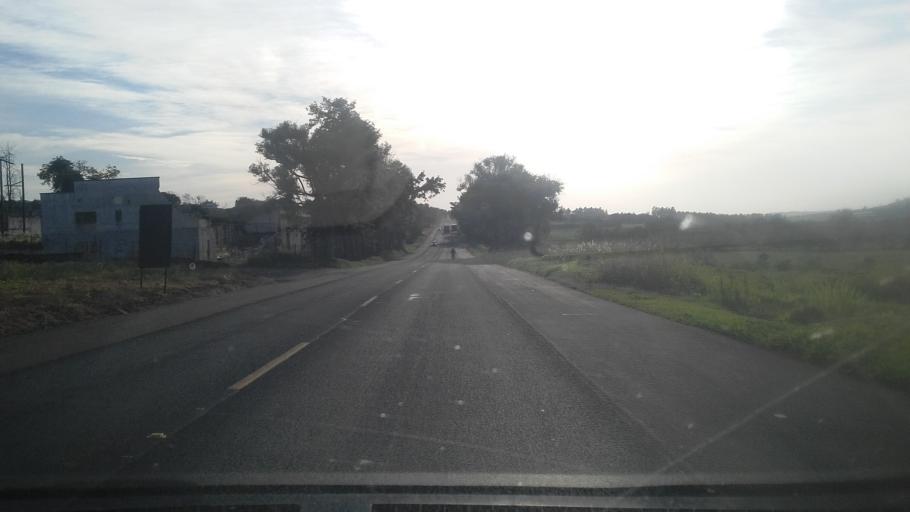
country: BR
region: Parana
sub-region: Bandeirantes
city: Bandeirantes
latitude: -23.1542
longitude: -50.5188
